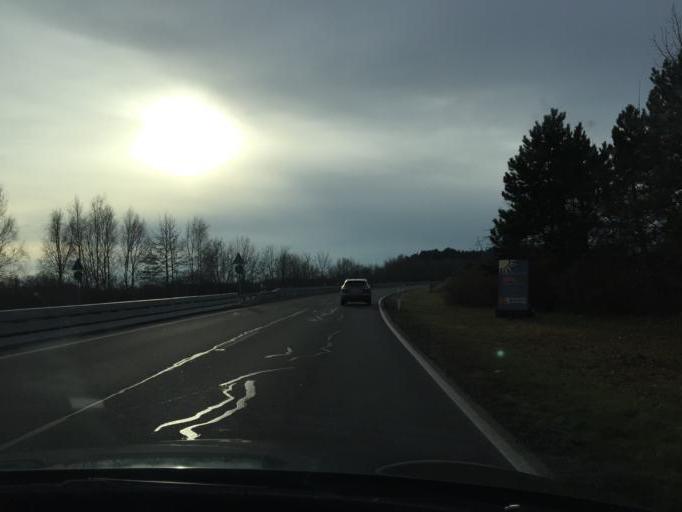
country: DE
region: Brandenburg
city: Peitz
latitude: 51.8110
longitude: 14.3902
